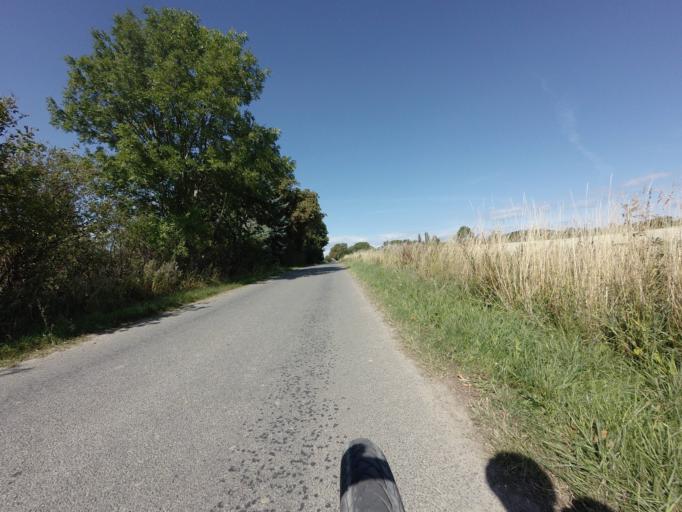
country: DK
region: Zealand
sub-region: Vordingborg Kommune
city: Stege
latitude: 55.0093
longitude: 12.4606
